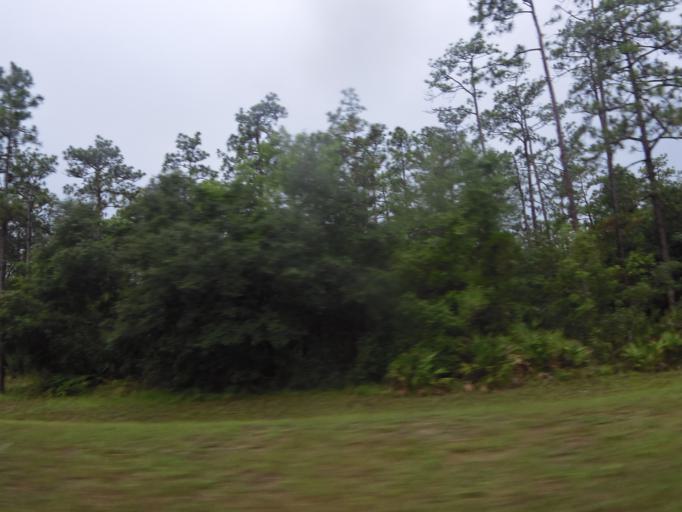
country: US
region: Florida
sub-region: Duval County
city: Jacksonville Beach
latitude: 30.2625
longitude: -81.4990
